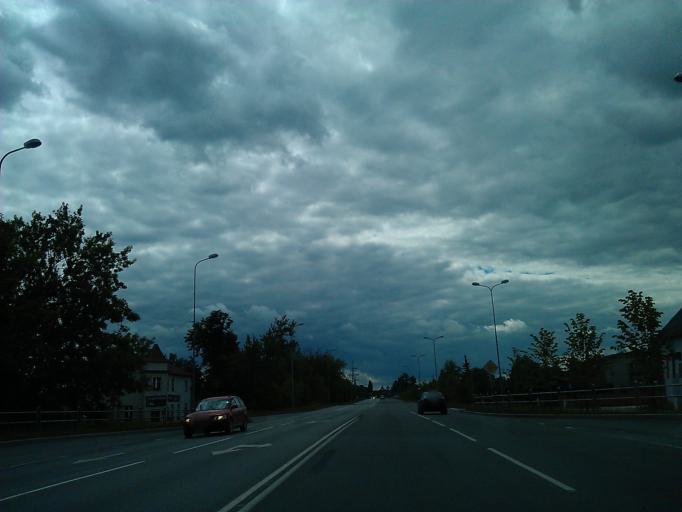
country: LV
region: Jelgava
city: Jelgava
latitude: 56.6351
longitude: 23.7280
